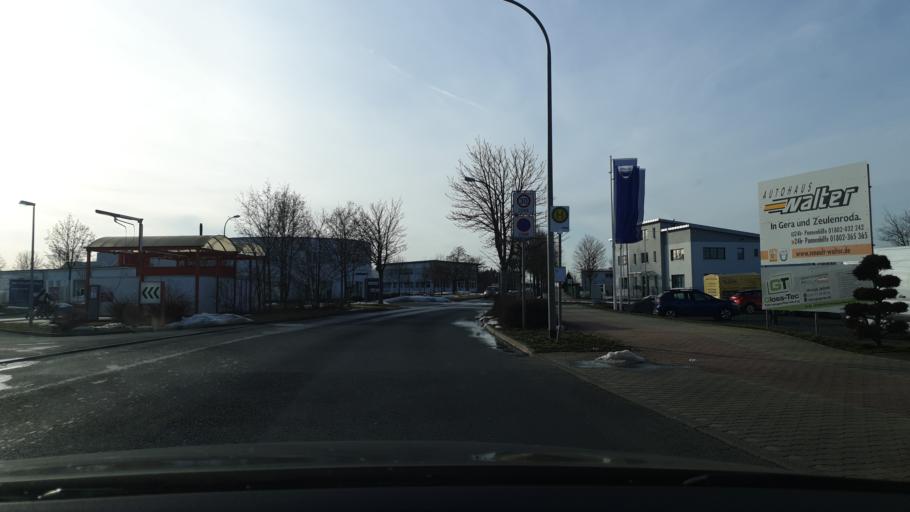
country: DE
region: Thuringia
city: Zeulenroda
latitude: 50.6613
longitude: 11.9965
